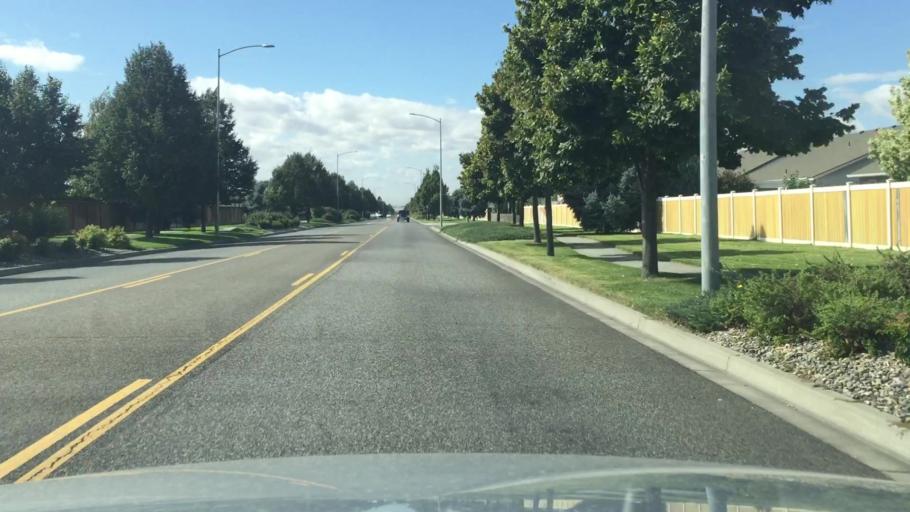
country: US
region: Washington
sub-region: Franklin County
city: West Pasco
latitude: 46.2780
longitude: -119.1929
